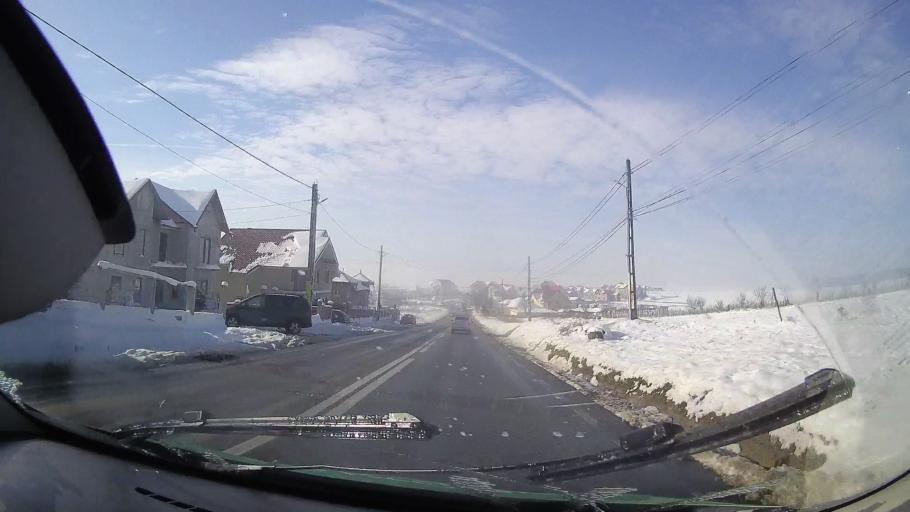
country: RO
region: Iasi
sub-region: Comuna Motca
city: Motca
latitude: 47.2544
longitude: 26.6141
